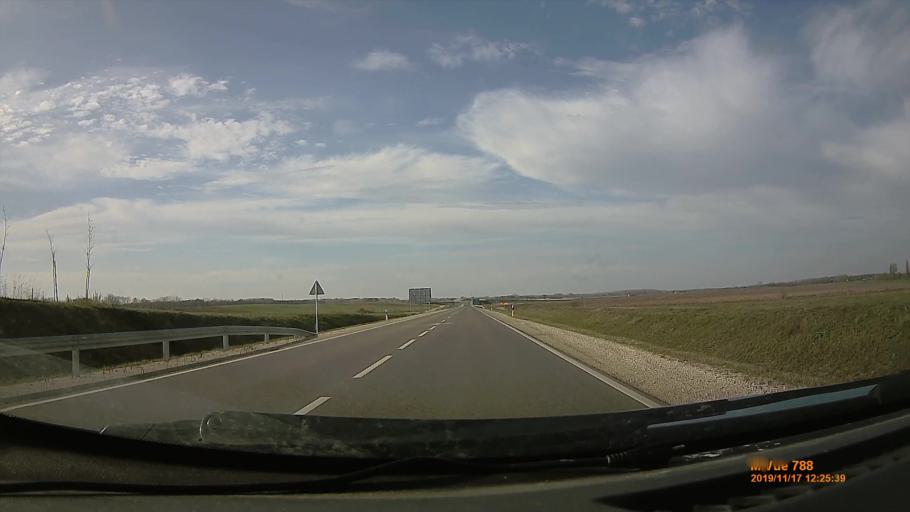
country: HU
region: Bacs-Kiskun
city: Kecskemet
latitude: 46.9311
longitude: 19.6301
